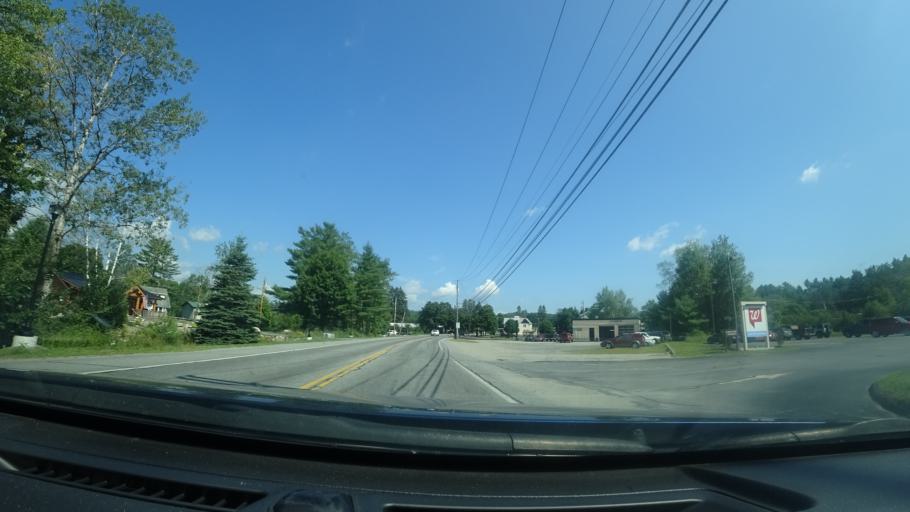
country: US
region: New York
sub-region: Warren County
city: Warrensburg
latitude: 43.6476
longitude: -73.8008
